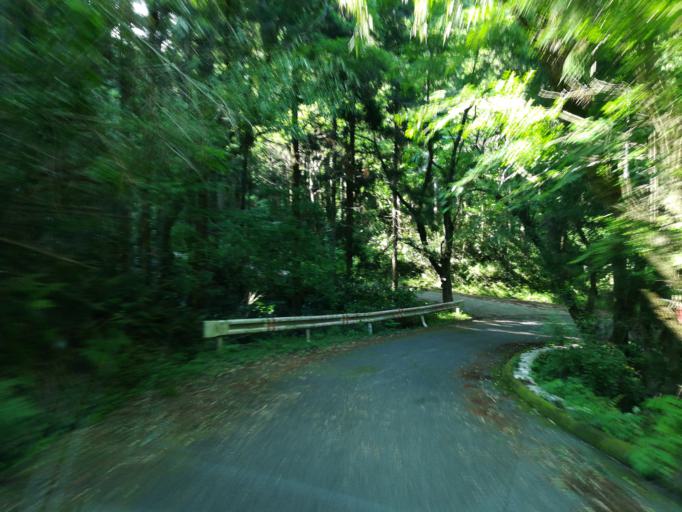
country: JP
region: Ibaraki
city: Tsukuba
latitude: 36.1869
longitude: 140.1381
